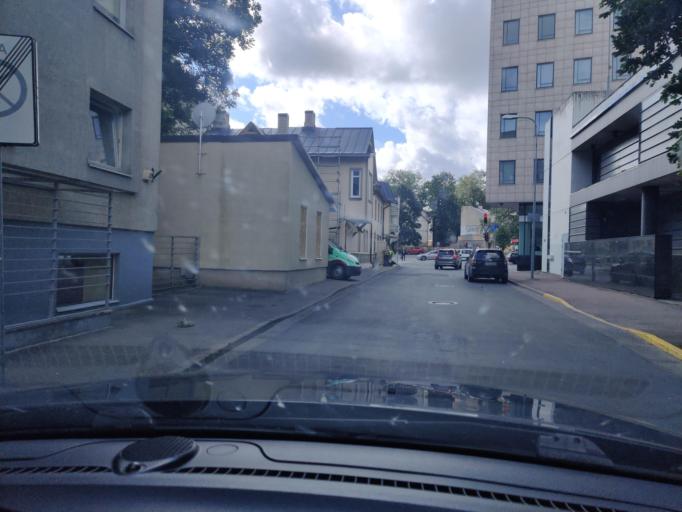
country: EE
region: Harju
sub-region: Tallinna linn
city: Tallinn
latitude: 59.4290
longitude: 24.7503
